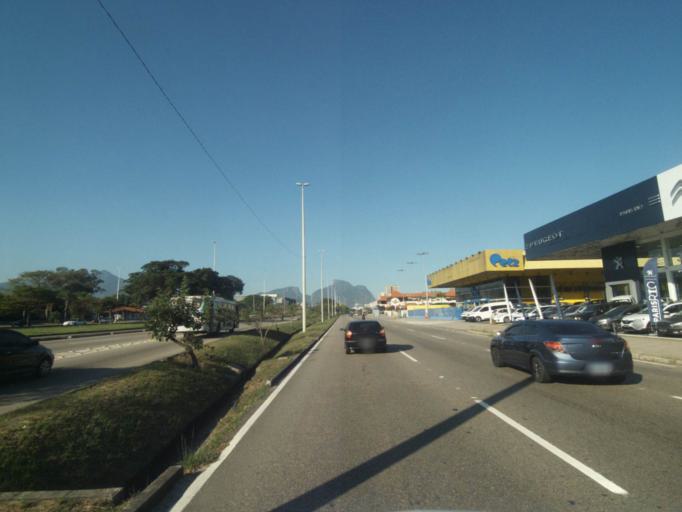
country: BR
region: Rio de Janeiro
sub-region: Rio De Janeiro
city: Rio de Janeiro
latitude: -23.0005
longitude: -43.3732
